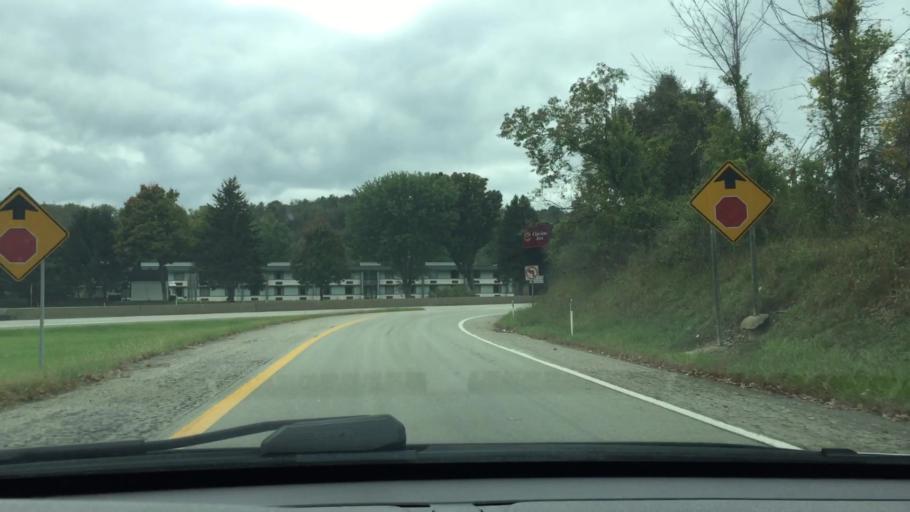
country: US
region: Pennsylvania
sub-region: Westmoreland County
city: Fellsburg
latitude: 40.1552
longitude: -79.7781
